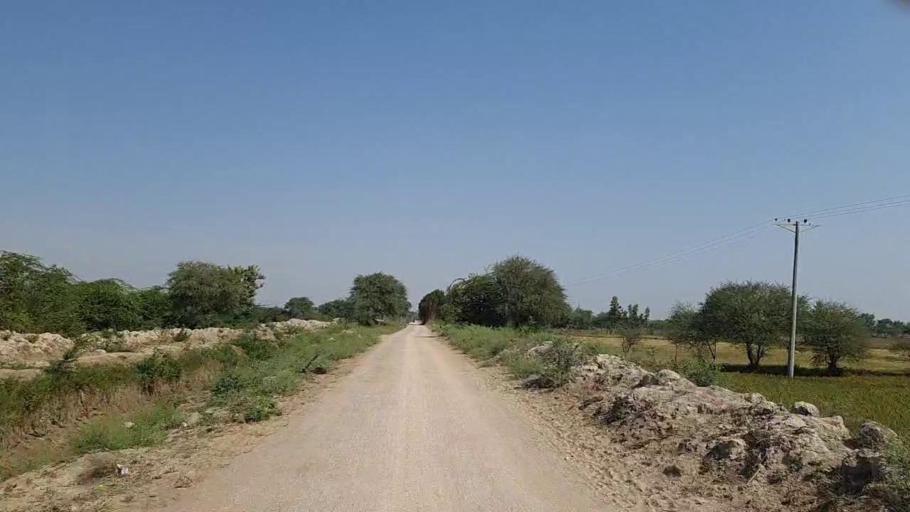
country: PK
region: Sindh
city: Mirpur Batoro
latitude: 24.6862
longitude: 68.2578
